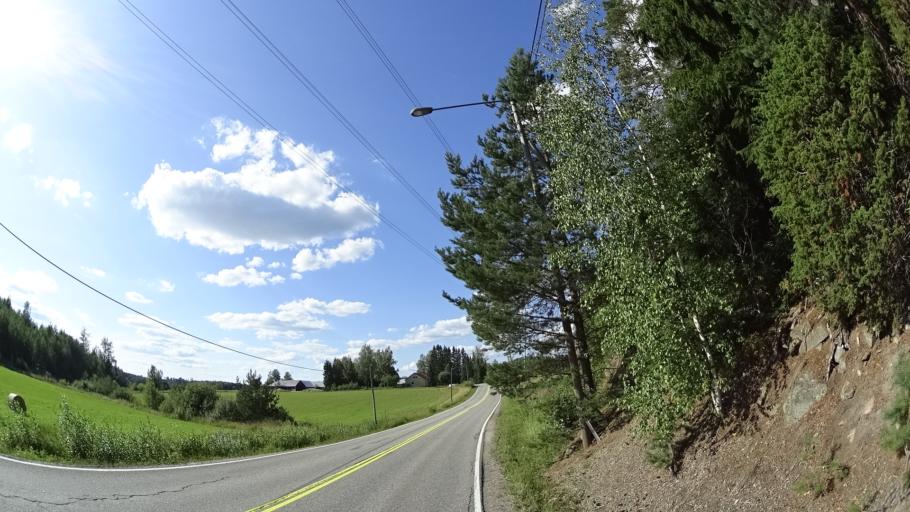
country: FI
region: Uusimaa
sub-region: Helsinki
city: Vihti
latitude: 60.3774
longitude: 24.3583
